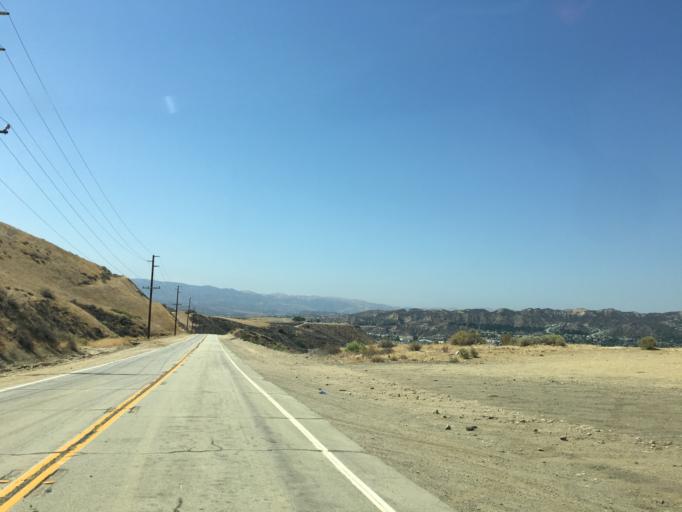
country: US
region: California
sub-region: Los Angeles County
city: Castaic
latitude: 34.5070
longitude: -118.6027
